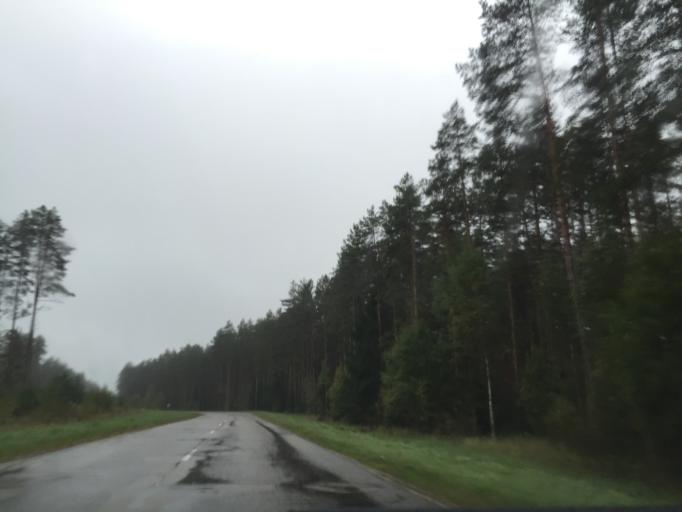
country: LV
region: Incukalns
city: Incukalns
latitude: 57.0397
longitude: 24.6777
